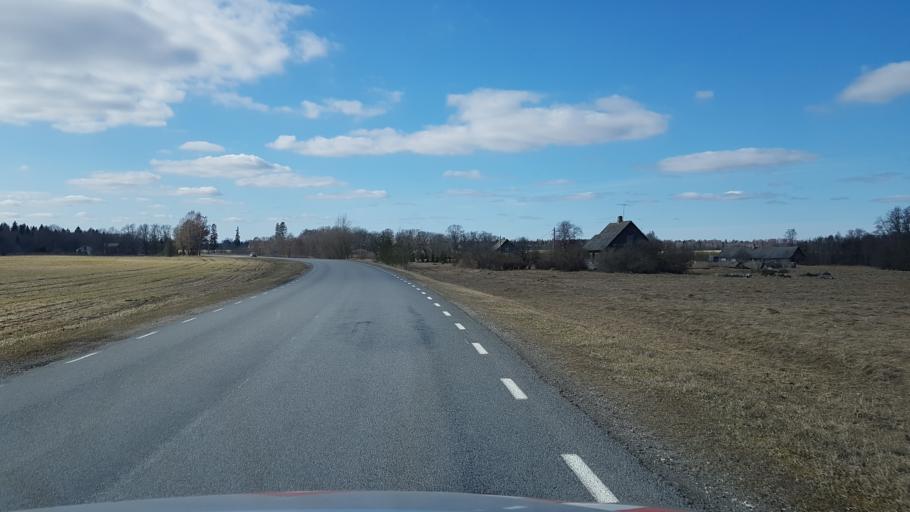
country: EE
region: Laeaene-Virumaa
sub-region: Tamsalu vald
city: Tamsalu
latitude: 59.1844
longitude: 26.0429
